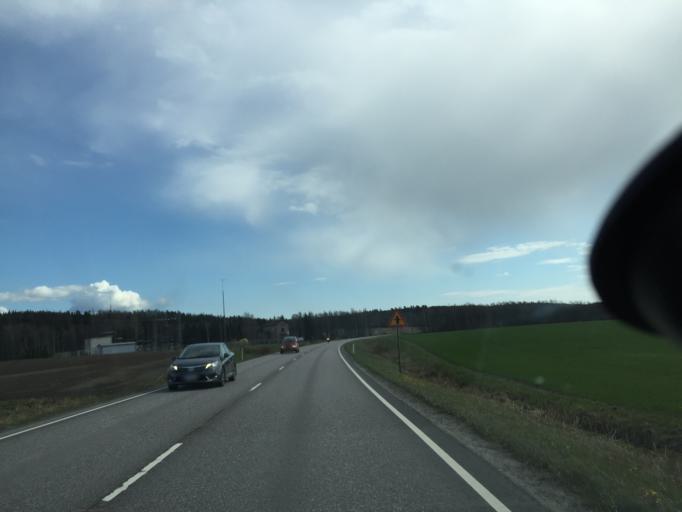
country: FI
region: Uusimaa
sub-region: Raaseporin
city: Ekenaes
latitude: 60.0567
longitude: 23.3278
